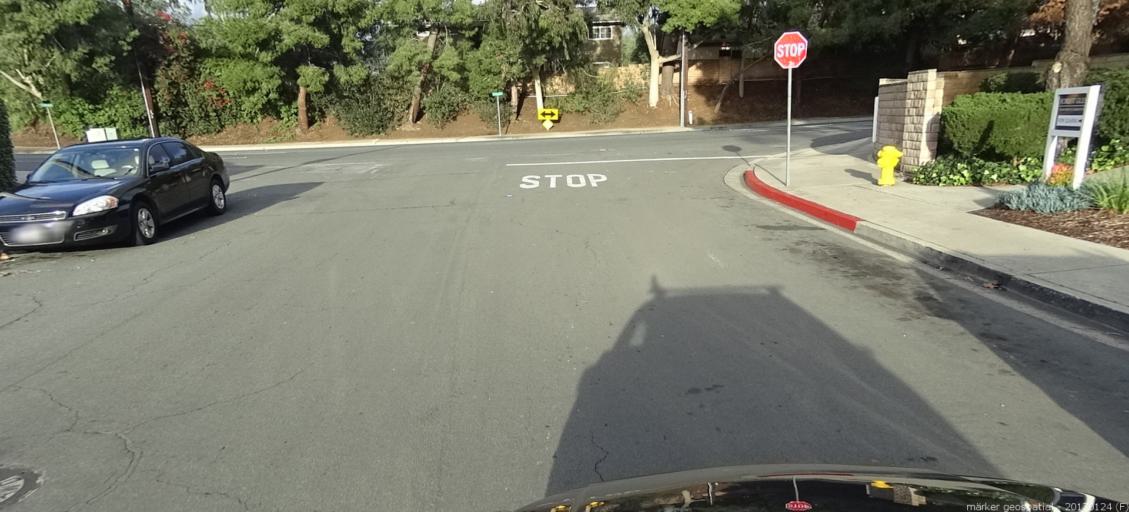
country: US
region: California
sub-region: Orange County
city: Lake Forest
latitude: 33.6293
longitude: -117.6921
